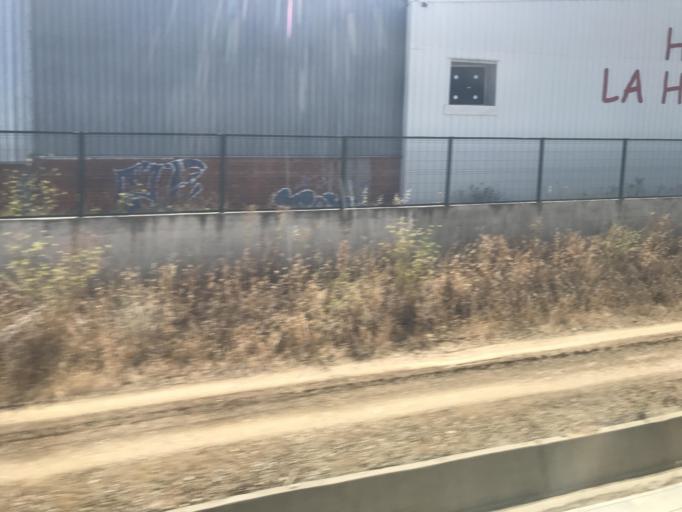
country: ES
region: Castille and Leon
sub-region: Provincia de Valladolid
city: Santovenia de Pisuerga
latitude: 41.6908
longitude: -4.6832
